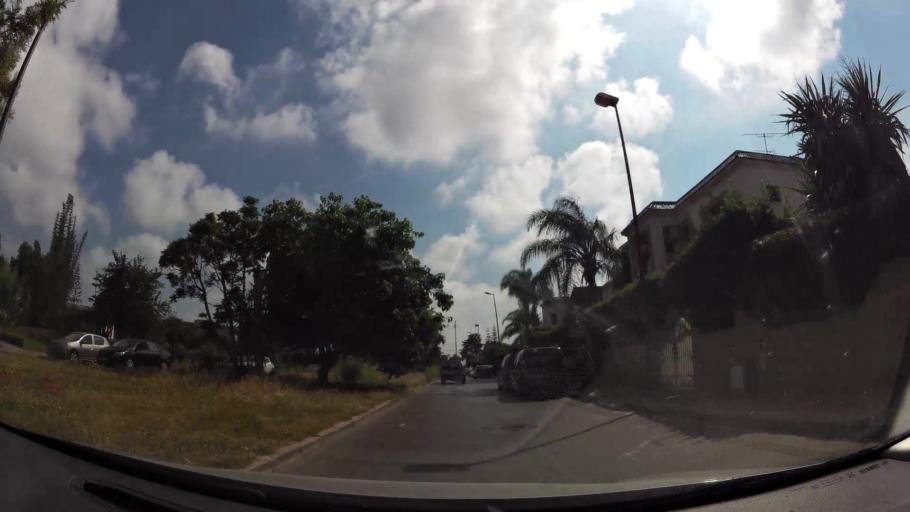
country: MA
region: Rabat-Sale-Zemmour-Zaer
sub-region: Skhirate-Temara
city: Temara
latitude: 33.9667
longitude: -6.8667
